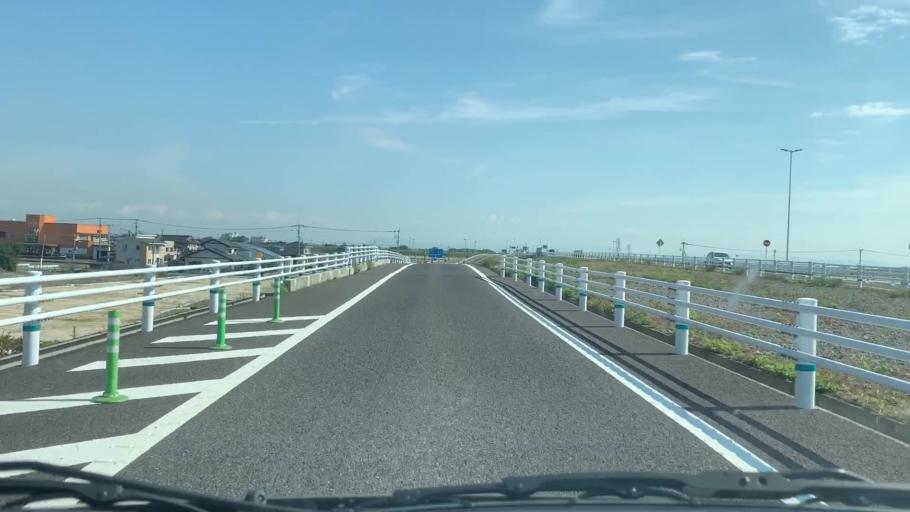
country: JP
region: Saga Prefecture
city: Saga-shi
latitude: 33.2313
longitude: 130.2377
